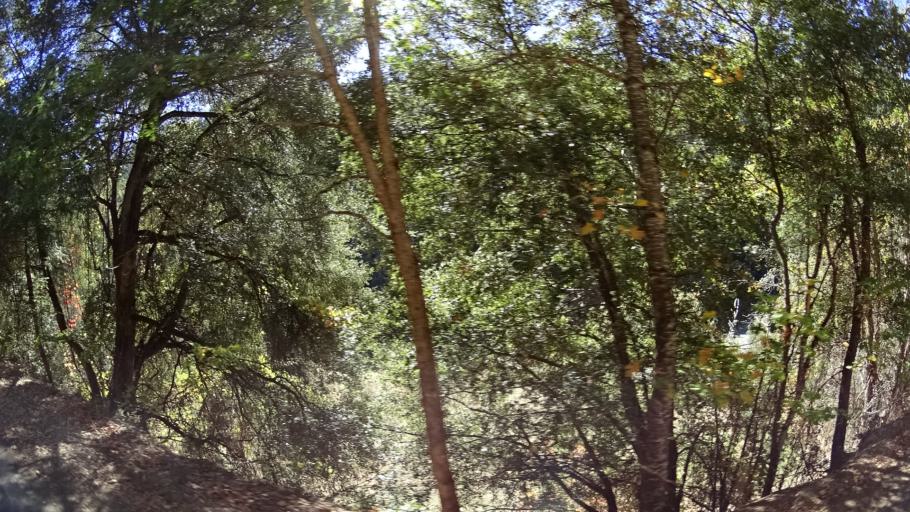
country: US
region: California
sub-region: Humboldt County
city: Willow Creek
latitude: 41.2855
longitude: -123.3612
